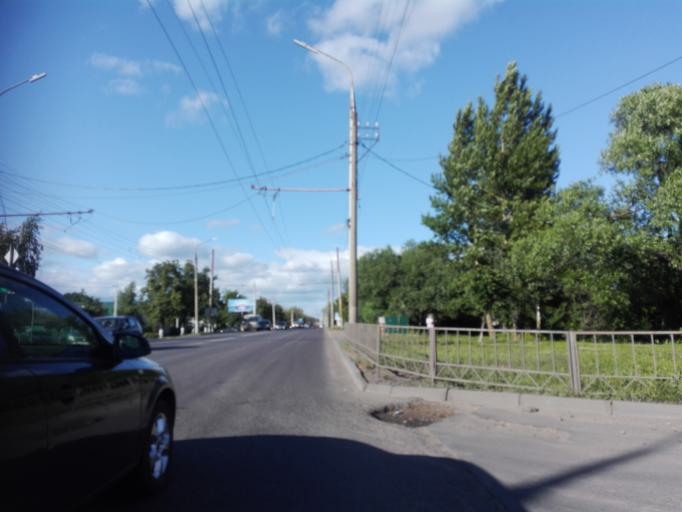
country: RU
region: Orjol
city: Orel
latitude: 52.9913
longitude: 36.1251
